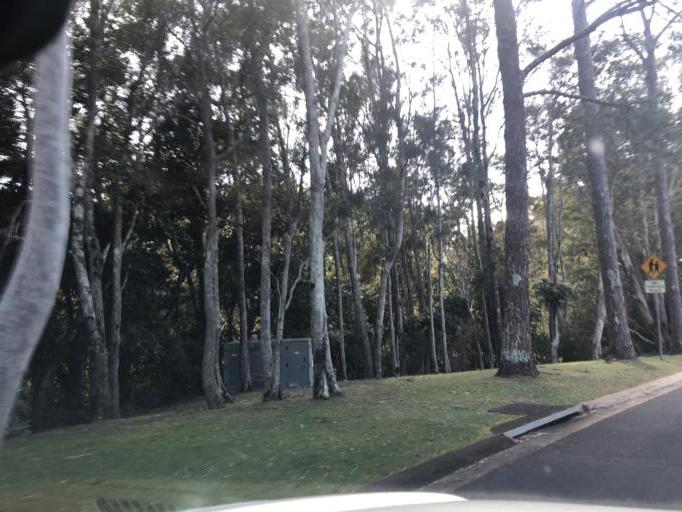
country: AU
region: New South Wales
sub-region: Coffs Harbour
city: Moonee Beach
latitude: -30.2301
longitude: 153.1509
